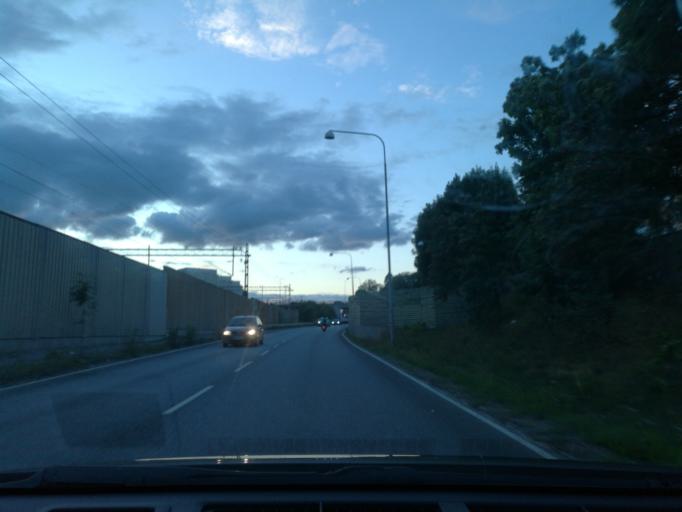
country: SE
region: Stockholm
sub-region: Solna Kommun
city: Solna
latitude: 59.3752
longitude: 18.0051
